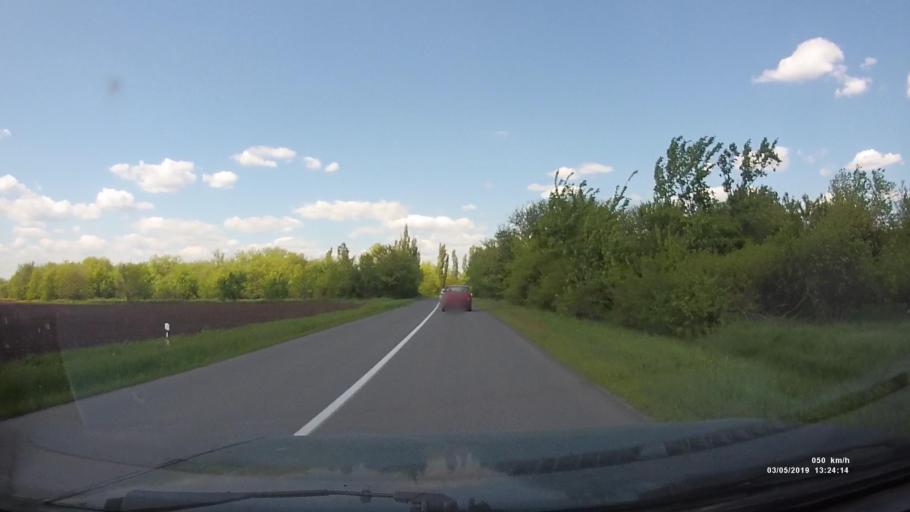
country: RU
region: Rostov
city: Semikarakorsk
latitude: 47.5633
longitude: 40.7956
